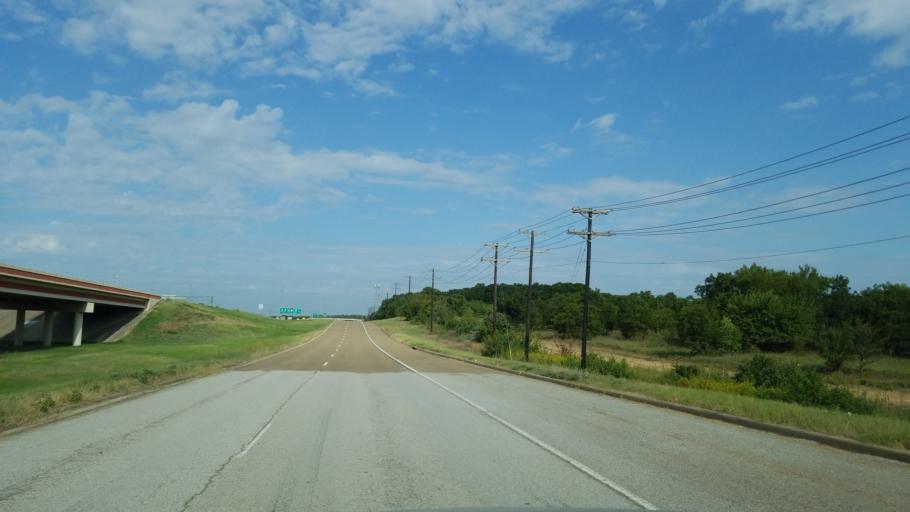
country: US
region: Texas
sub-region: Tarrant County
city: Grapevine
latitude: 32.8961
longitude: -97.0865
